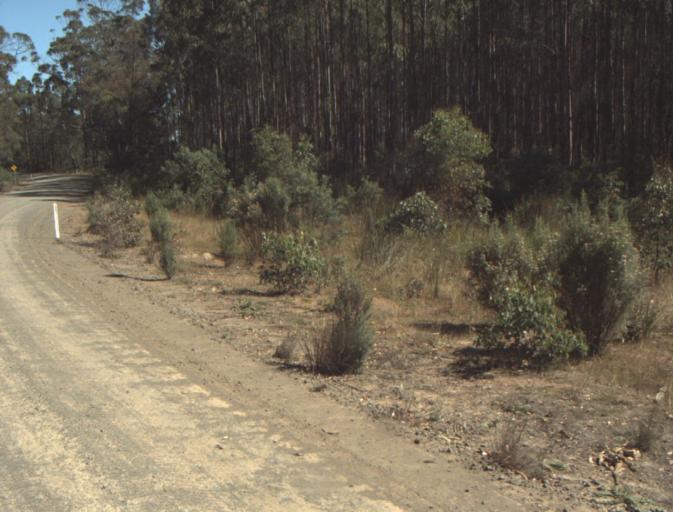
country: AU
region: Tasmania
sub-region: Launceston
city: Newstead
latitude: -41.3694
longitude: 147.2391
